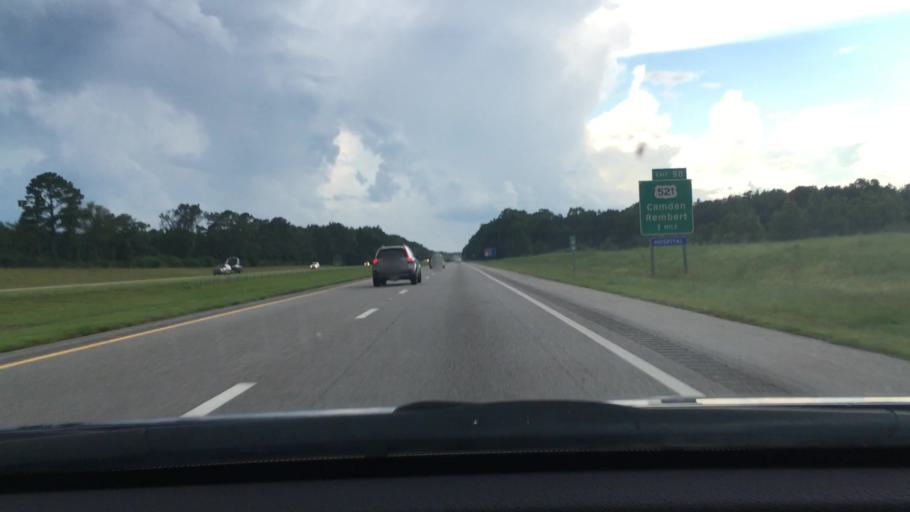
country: US
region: South Carolina
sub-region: Kershaw County
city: Camden
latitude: 34.2148
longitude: -80.5713
